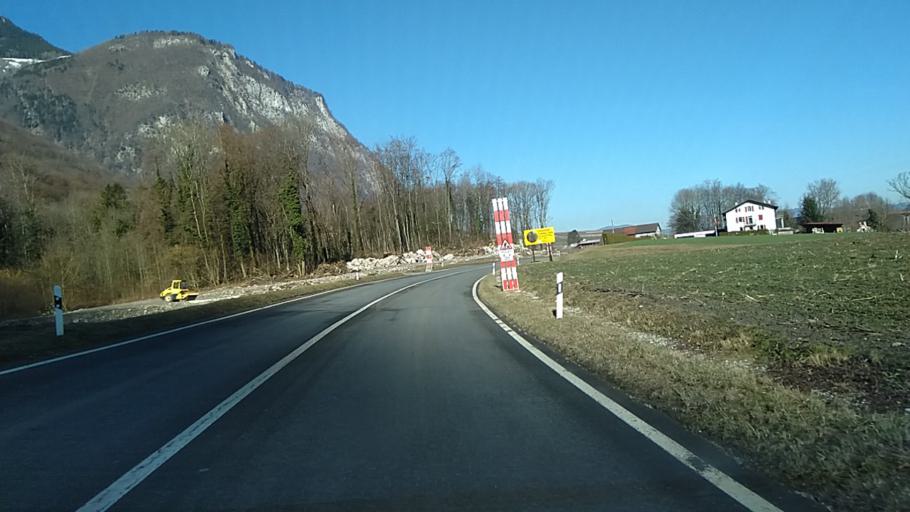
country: CH
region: Valais
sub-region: Monthey District
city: Vouvry
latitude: 46.3529
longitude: 6.8797
